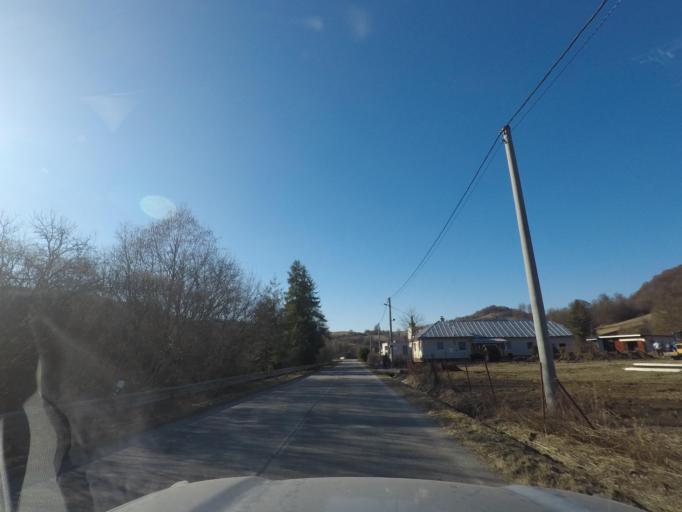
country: PL
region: Subcarpathian Voivodeship
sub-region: Powiat sanocki
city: Komancza
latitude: 49.1626
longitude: 22.0426
